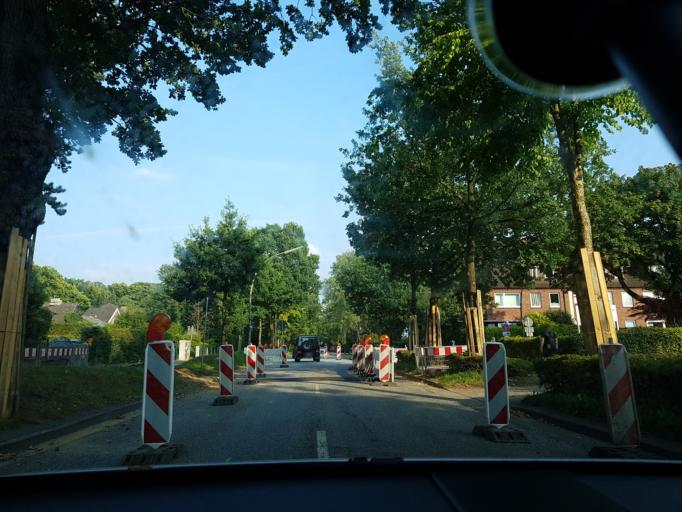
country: DE
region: Hamburg
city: Wellingsbuettel
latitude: 53.6402
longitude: 10.0851
